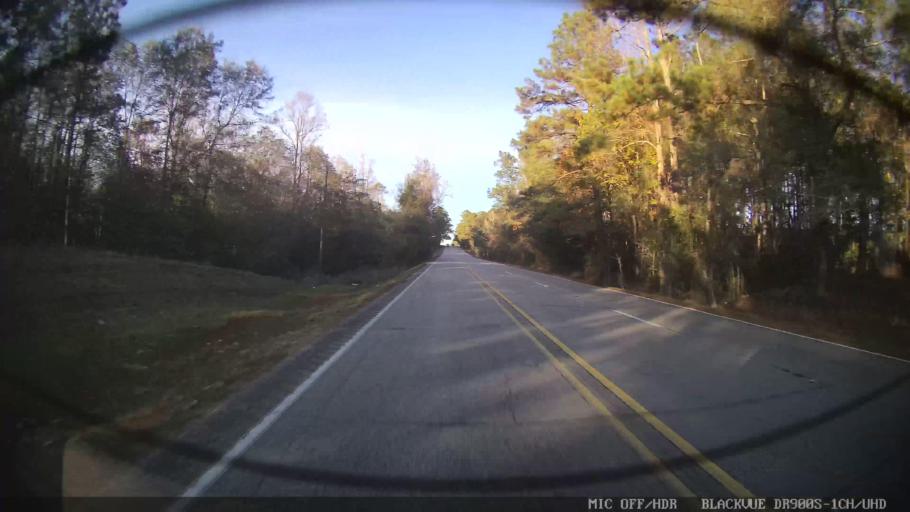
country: US
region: Mississippi
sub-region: Lamar County
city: Purvis
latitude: 31.0935
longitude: -89.4148
